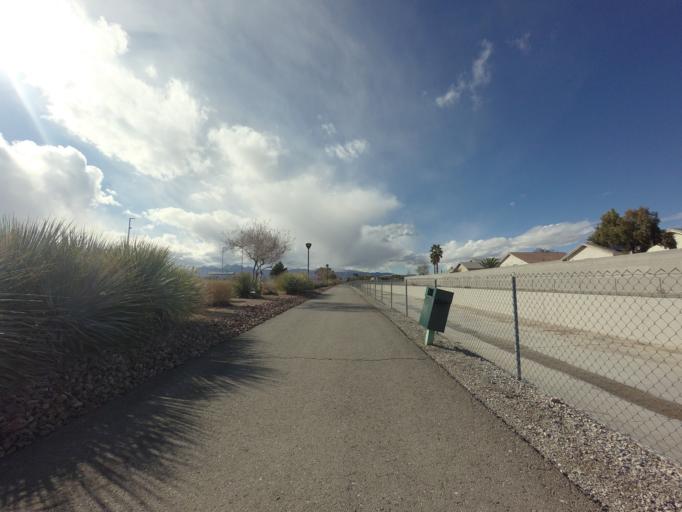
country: US
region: Nevada
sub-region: Clark County
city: North Las Vegas
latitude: 36.2578
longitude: -115.1765
